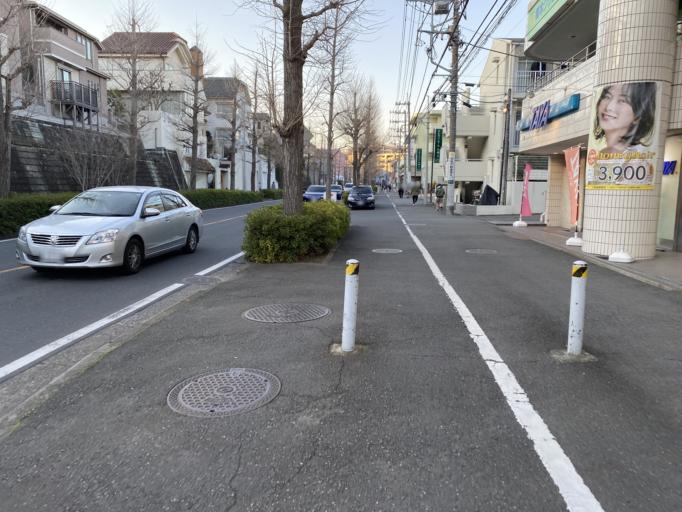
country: JP
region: Tokyo
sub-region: Machida-shi
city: Machida
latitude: 35.5440
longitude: 139.5131
